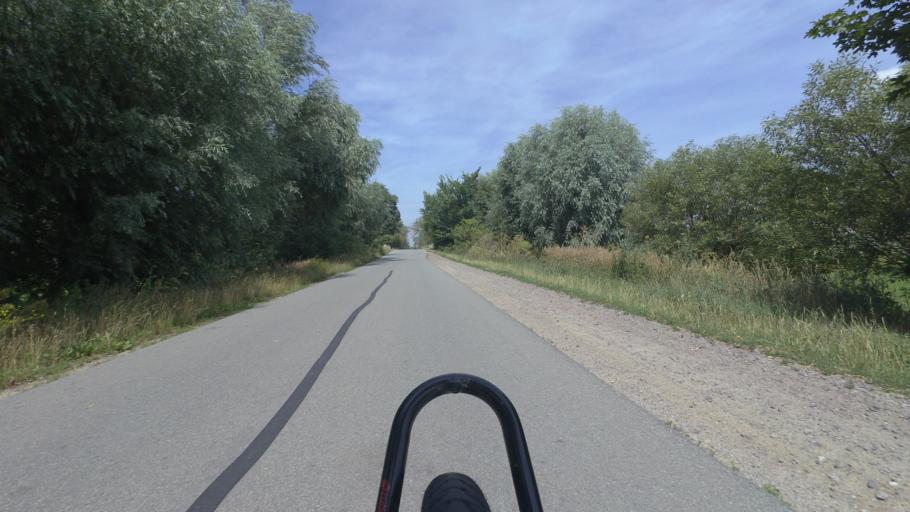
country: DE
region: Brandenburg
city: Rhinow
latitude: 52.7578
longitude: 12.3336
